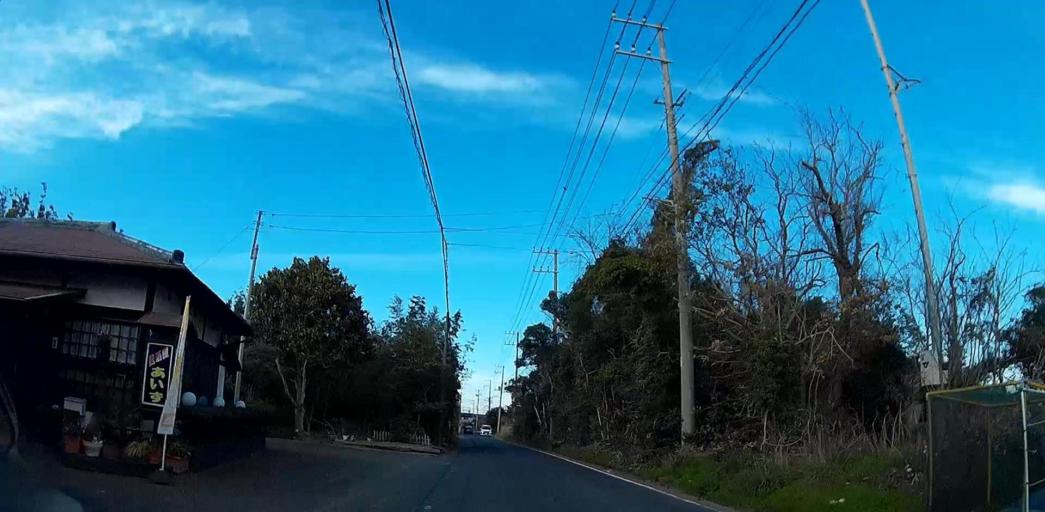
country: JP
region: Chiba
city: Hasaki
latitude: 35.7986
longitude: 140.7838
